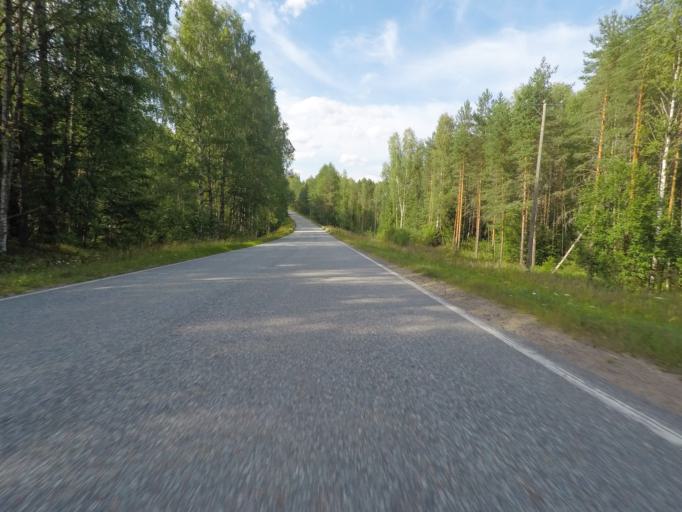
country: FI
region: Southern Savonia
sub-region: Savonlinna
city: Sulkava
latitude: 61.7175
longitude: 28.2094
